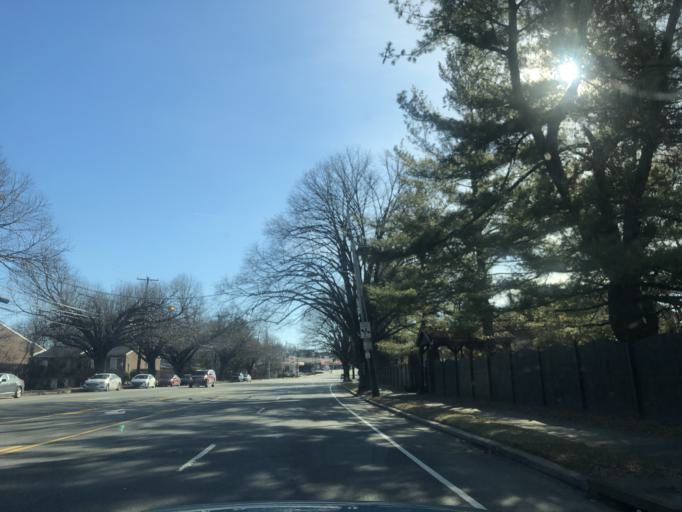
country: US
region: Pennsylvania
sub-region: Montgomery County
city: Flourtown
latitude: 40.0723
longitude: -75.2423
